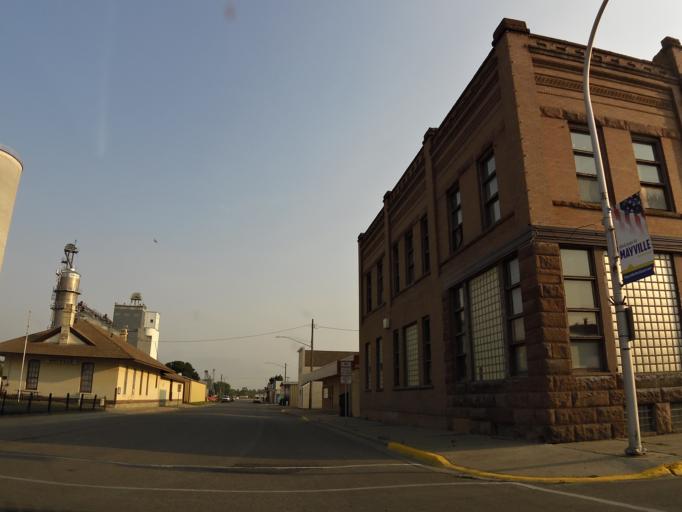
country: US
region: North Dakota
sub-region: Traill County
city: Mayville
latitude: 47.5006
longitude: -97.3251
